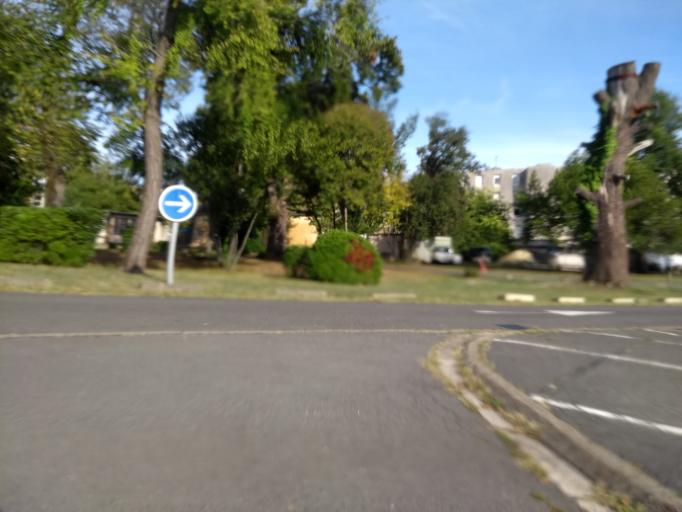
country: FR
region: Aquitaine
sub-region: Departement de la Gironde
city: Talence
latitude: 44.8100
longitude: -0.5928
